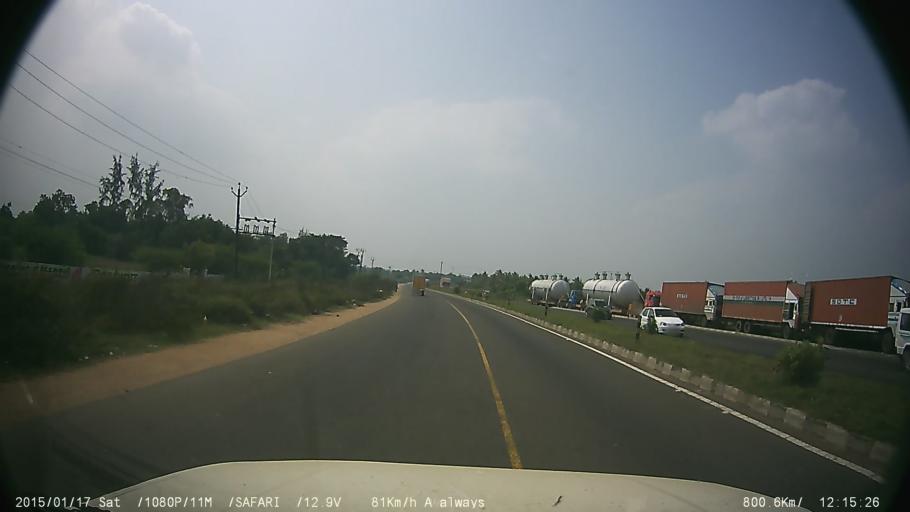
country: IN
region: Tamil Nadu
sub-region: Kancheepuram
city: Sriperumbudur
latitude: 12.9223
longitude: 79.8737
